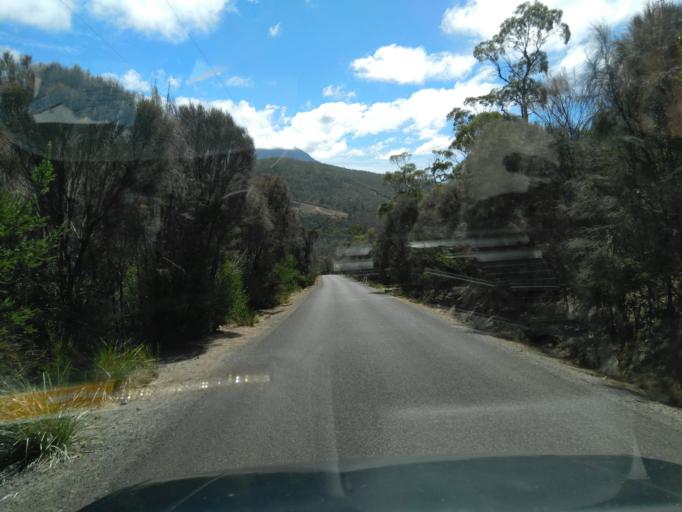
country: AU
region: Tasmania
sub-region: Kingborough
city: Kingston
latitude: -42.9494
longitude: 147.3161
